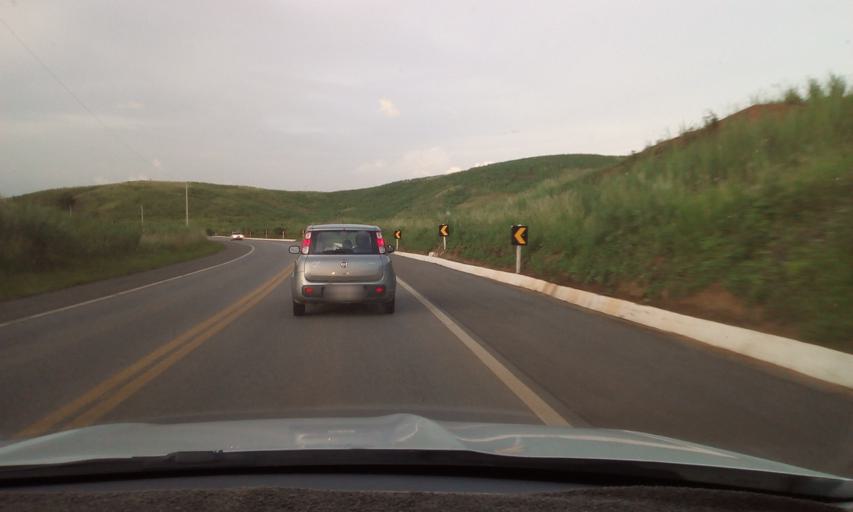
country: BR
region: Pernambuco
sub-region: Vicencia
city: Vicencia
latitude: -7.6250
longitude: -35.2419
